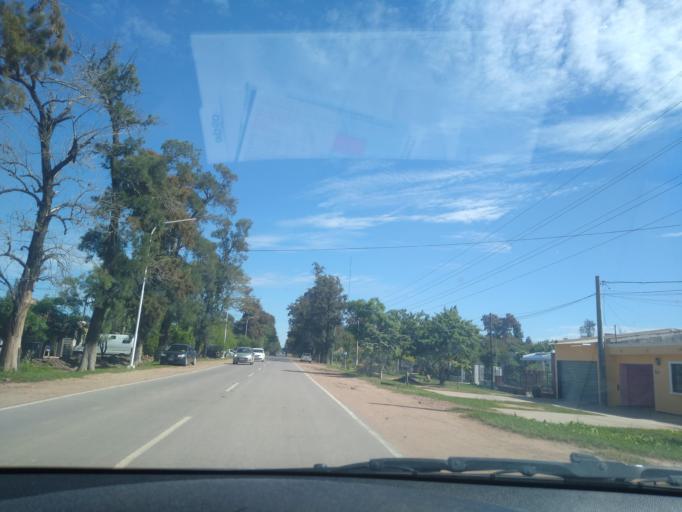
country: AR
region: Chaco
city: Presidencia Roque Saenz Pena
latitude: -26.7742
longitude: -60.4145
